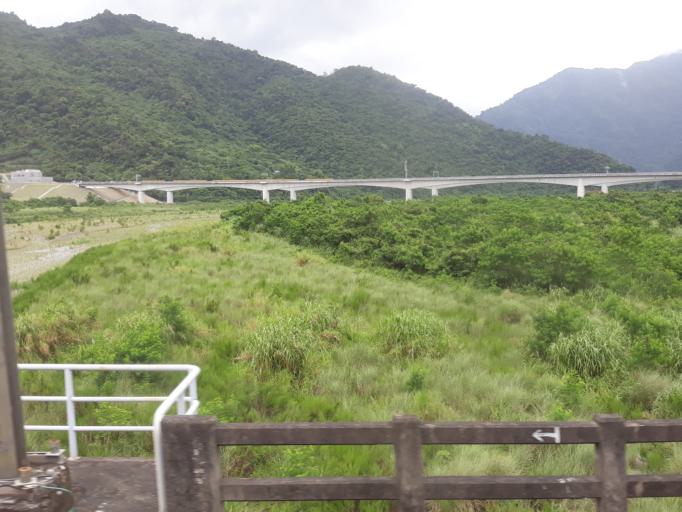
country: TW
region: Taiwan
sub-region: Yilan
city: Yilan
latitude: 24.4422
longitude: 121.7793
